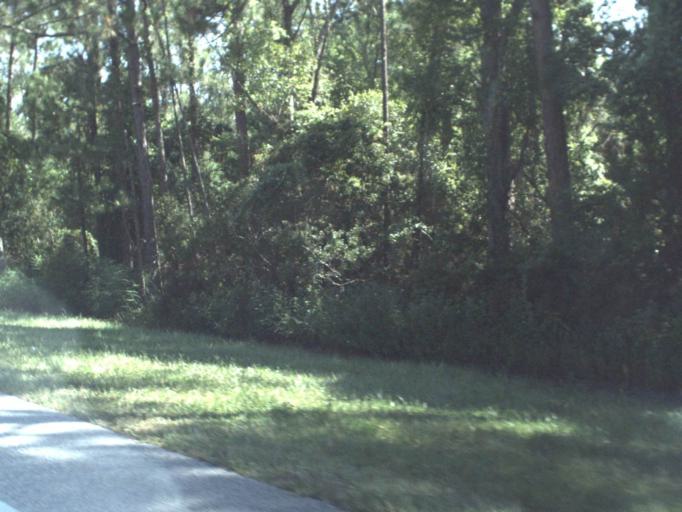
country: US
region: Florida
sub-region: Alachua County
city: Hawthorne
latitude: 29.6892
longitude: -82.1277
